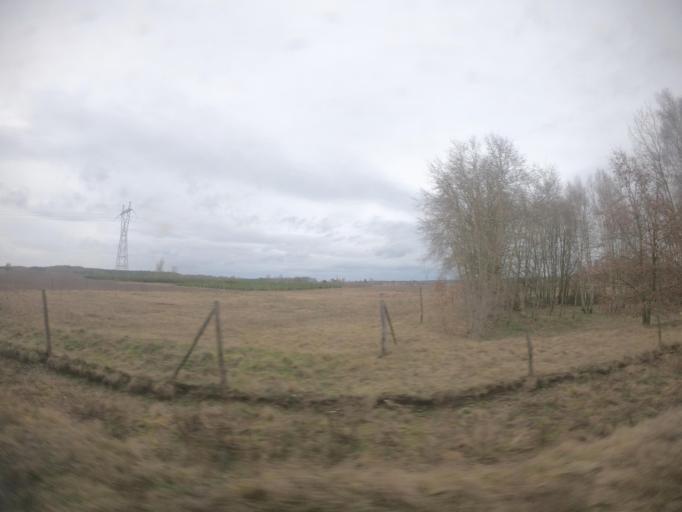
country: PL
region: West Pomeranian Voivodeship
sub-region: Powiat szczecinecki
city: Szczecinek
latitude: 53.7259
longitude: 16.8114
